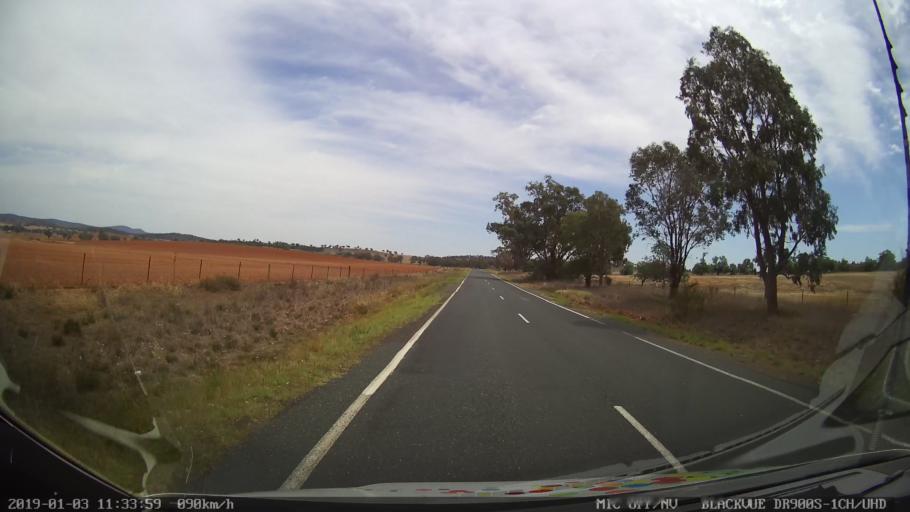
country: AU
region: New South Wales
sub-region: Weddin
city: Grenfell
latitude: -33.9403
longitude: 148.1670
